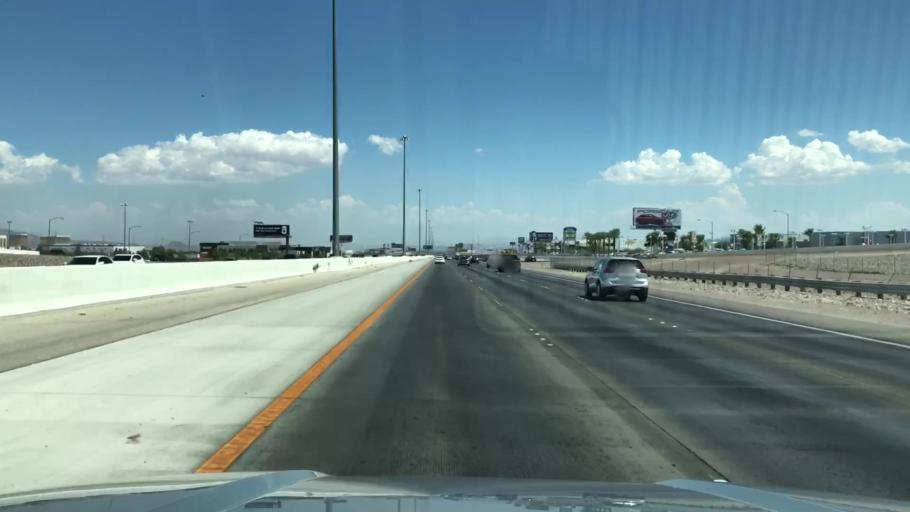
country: US
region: Nevada
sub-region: Clark County
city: Enterprise
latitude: 36.0666
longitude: -115.2408
